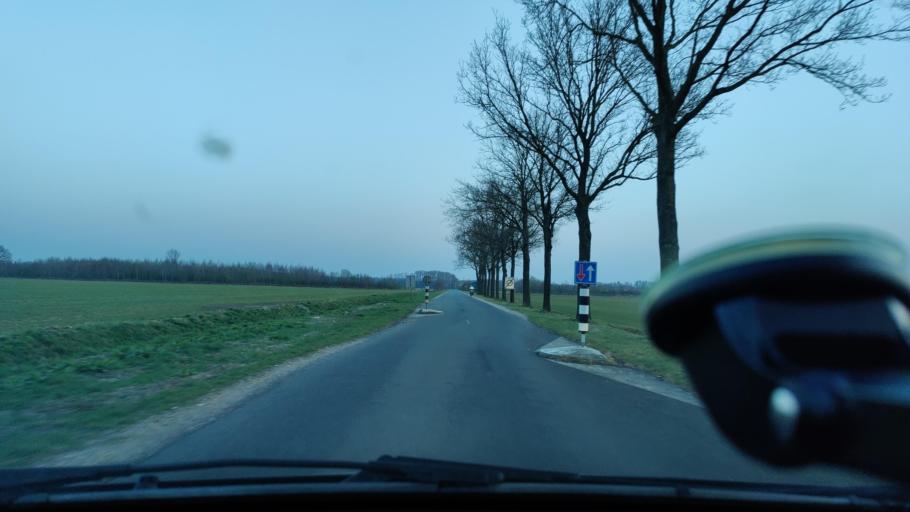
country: NL
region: Limburg
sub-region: Gemeente Bergen
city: Wellerlooi
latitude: 51.5373
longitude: 6.1738
